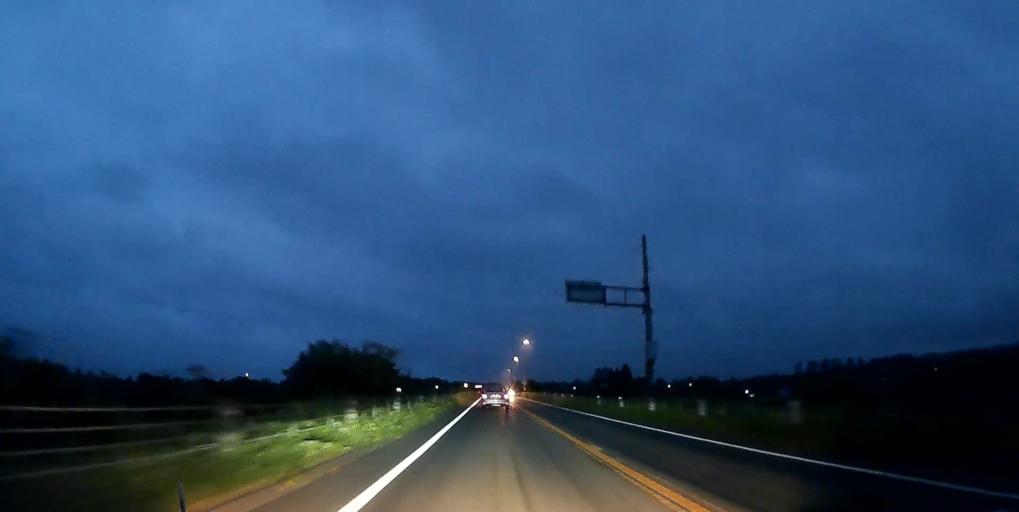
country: JP
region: Hokkaido
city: Nanae
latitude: 42.2109
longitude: 140.3935
